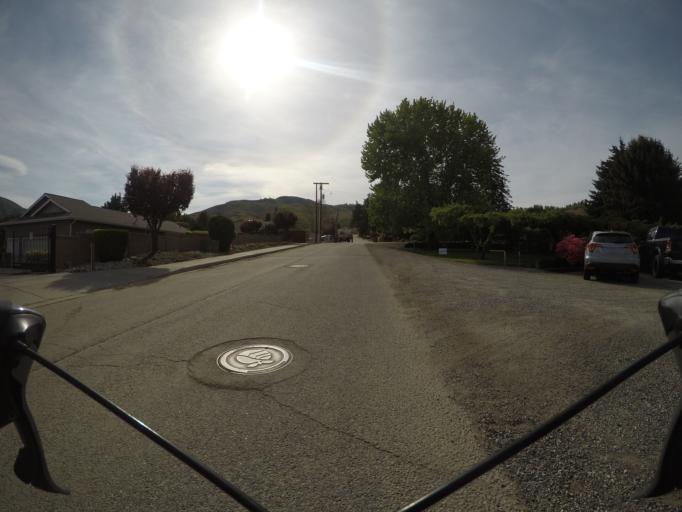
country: US
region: Washington
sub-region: Chelan County
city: West Wenatchee
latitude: 47.4426
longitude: -120.3510
